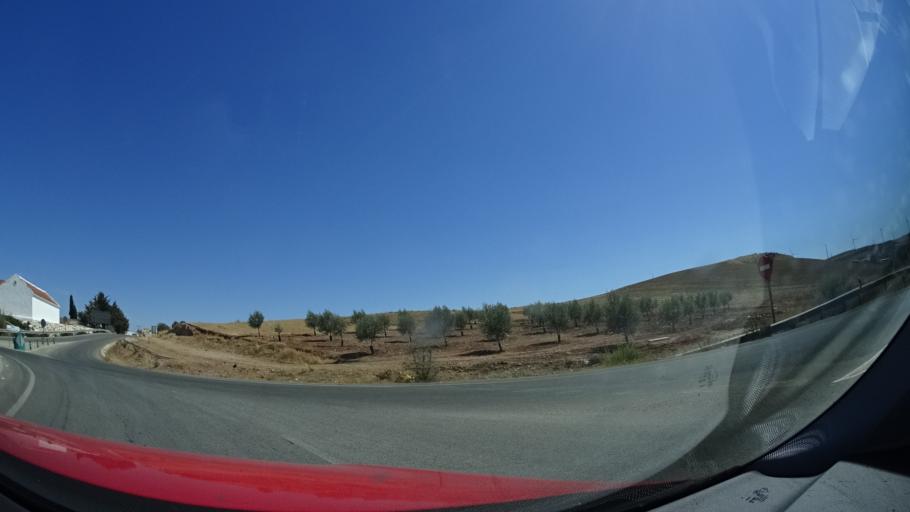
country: ES
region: Andalusia
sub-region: Provincia de Malaga
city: Sierra de Yeguas
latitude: 37.1240
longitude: -4.8768
